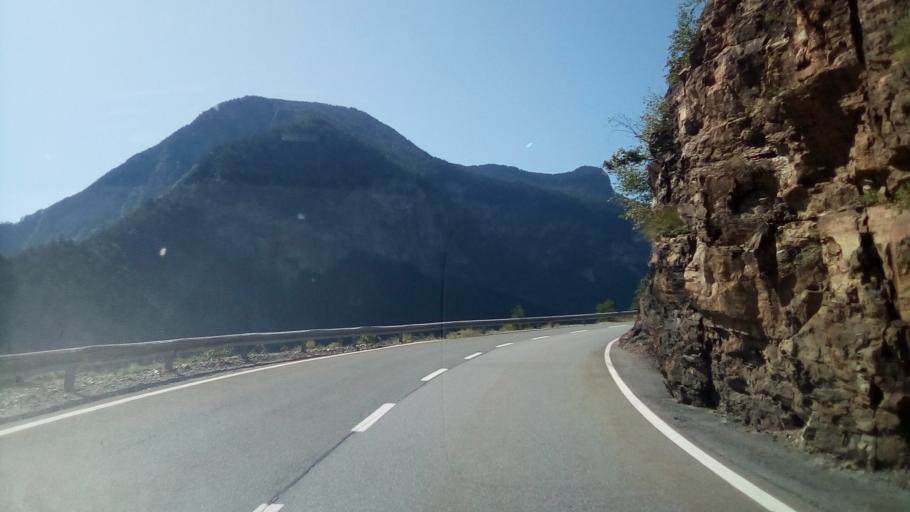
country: CH
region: Valais
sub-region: Saint-Maurice District
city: Vernayaz
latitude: 46.1266
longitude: 7.0343
